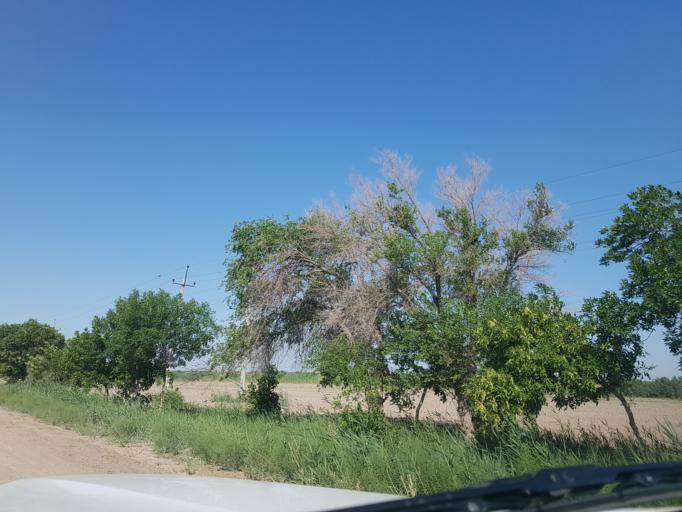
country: TM
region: Dasoguz
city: Koeneuergench
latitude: 42.1302
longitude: 58.9455
